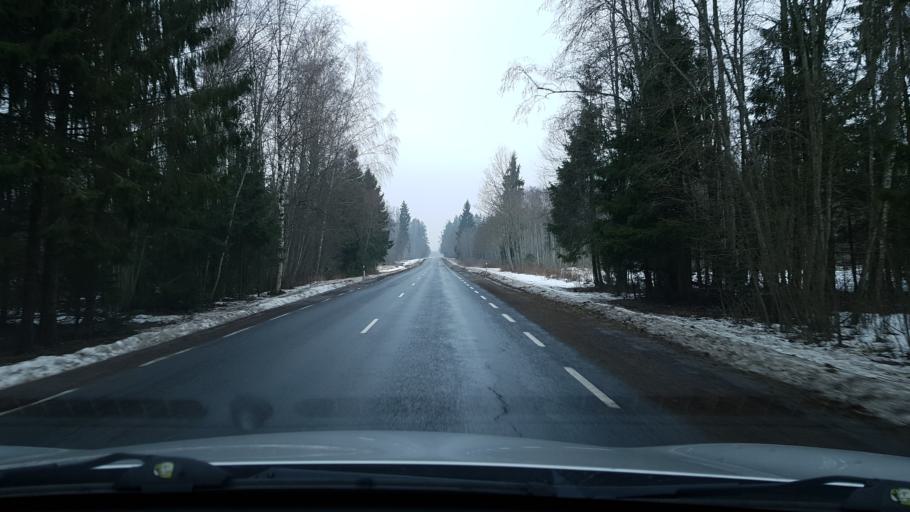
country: EE
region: Valgamaa
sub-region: Torva linn
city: Torva
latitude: 58.1743
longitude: 25.9609
